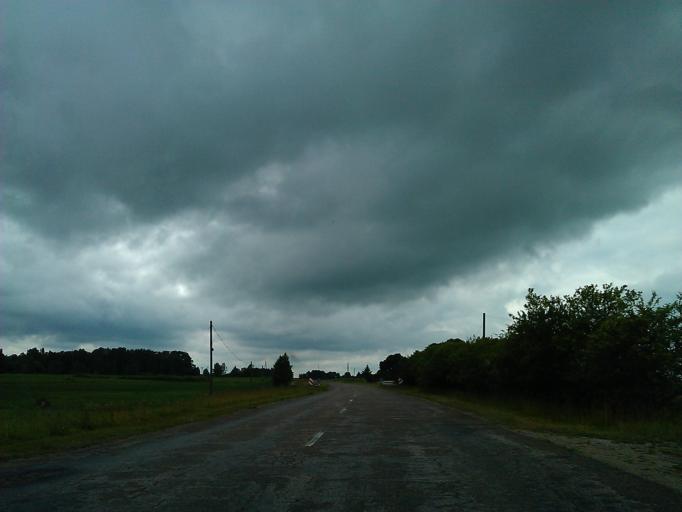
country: LV
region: Kuldigas Rajons
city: Kuldiga
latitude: 56.8531
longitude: 21.7973
